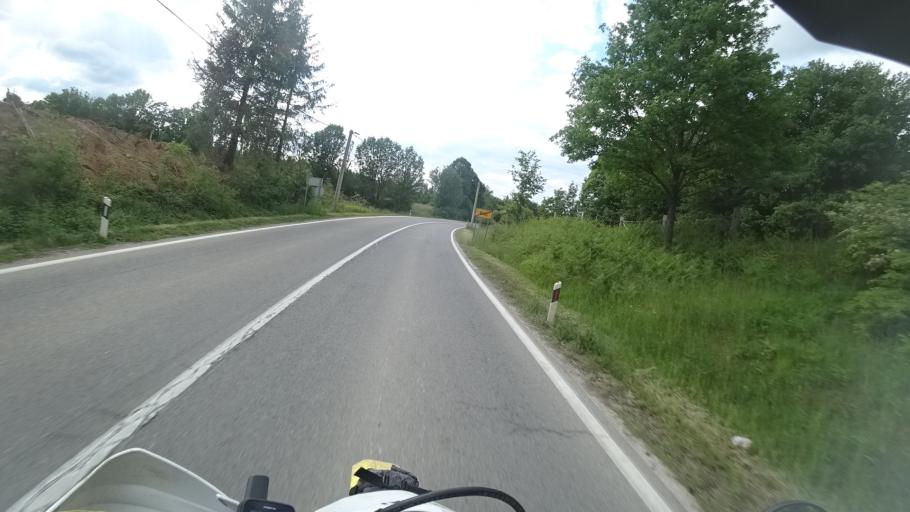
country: HR
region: Licko-Senjska
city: Gospic
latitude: 44.5175
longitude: 15.4170
